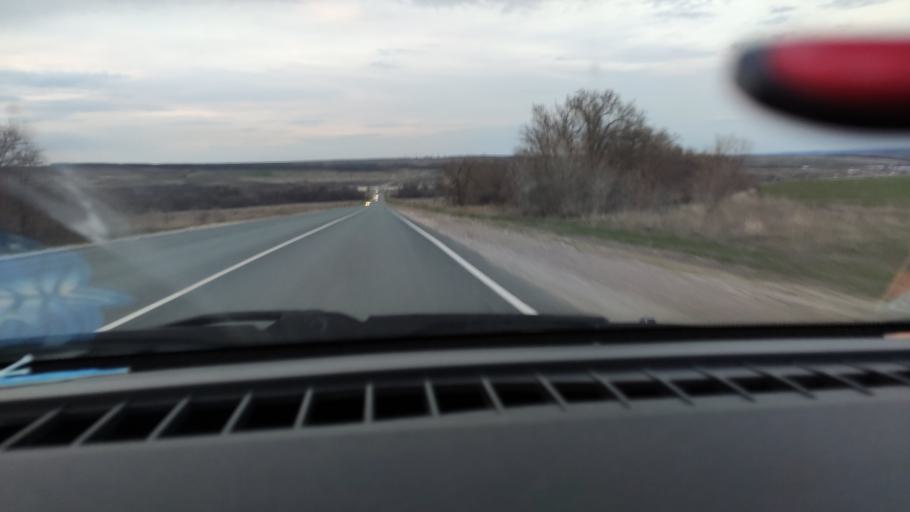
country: RU
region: Saratov
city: Sinodskoye
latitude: 51.9154
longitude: 46.5572
